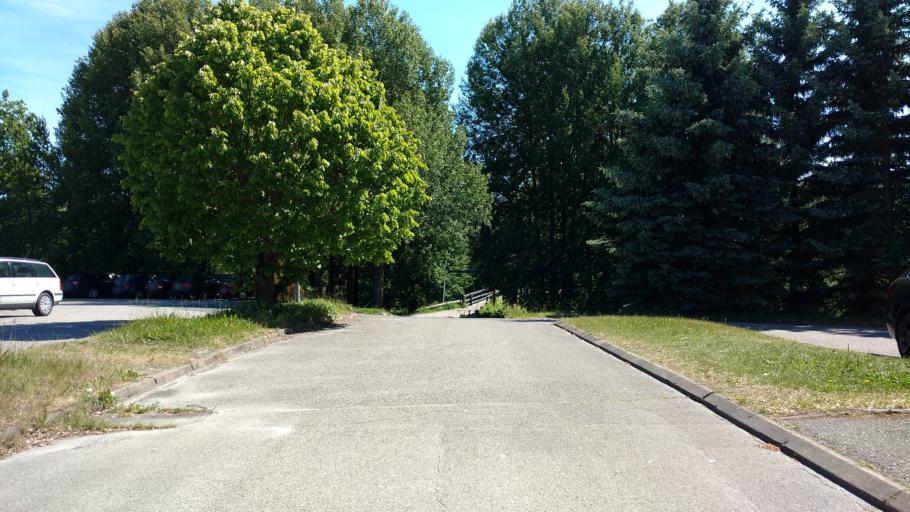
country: FI
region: Varsinais-Suomi
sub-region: Salo
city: Salo
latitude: 60.3919
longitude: 23.1304
